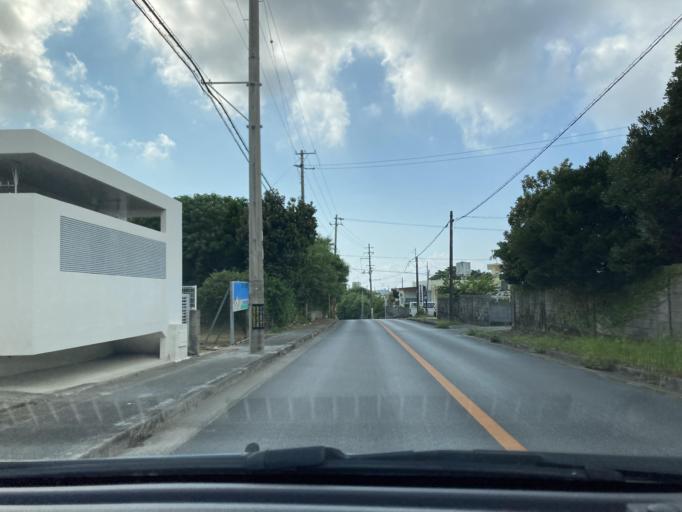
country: JP
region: Okinawa
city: Itoman
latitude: 26.1346
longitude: 127.7700
